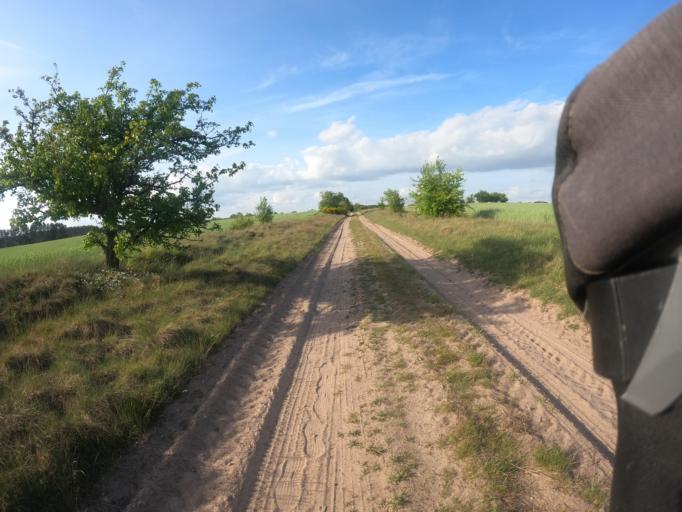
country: PL
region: West Pomeranian Voivodeship
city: Trzcinsko Zdroj
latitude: 52.8907
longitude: 14.7196
